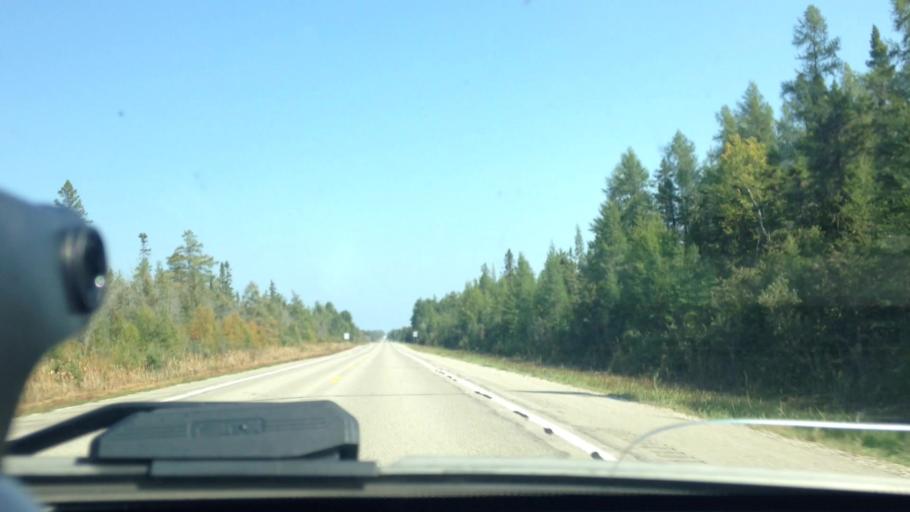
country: US
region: Michigan
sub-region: Luce County
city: Newberry
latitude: 46.3035
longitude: -85.3406
